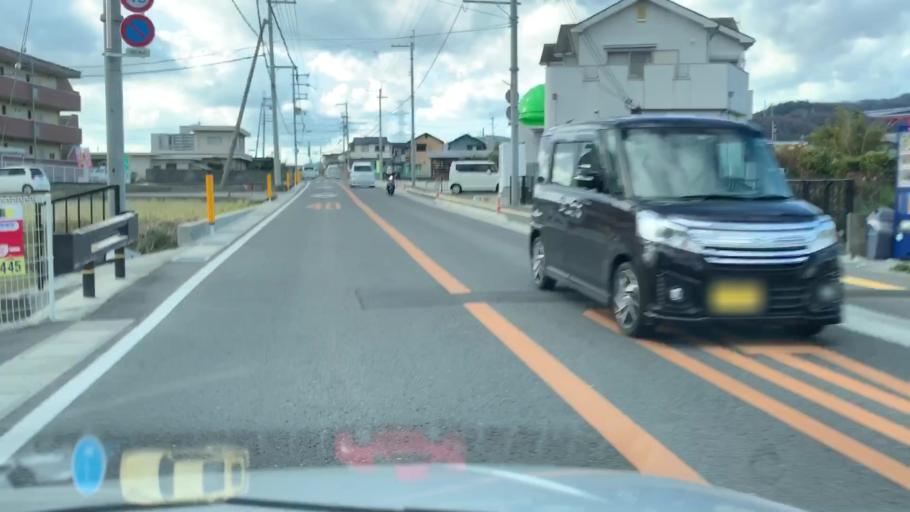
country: JP
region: Wakayama
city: Iwade
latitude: 34.2722
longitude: 135.2843
